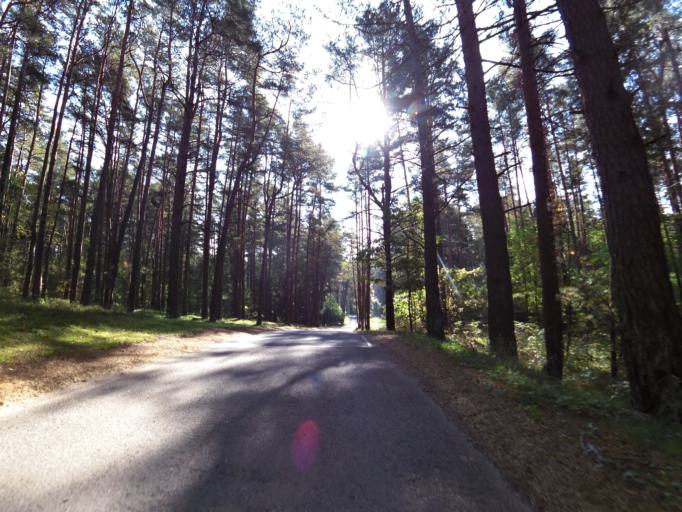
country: LT
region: Vilnius County
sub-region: Vilnius
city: Vilnius
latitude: 54.7353
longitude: 25.3084
